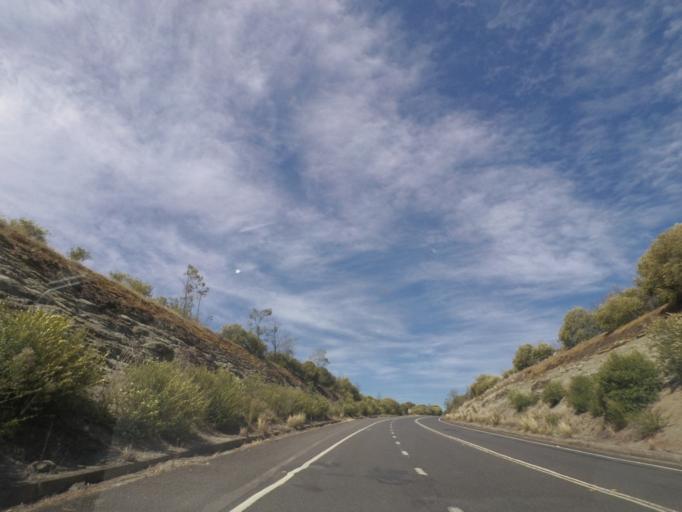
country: AU
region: New South Wales
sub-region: Wollondilly
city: Douglas Park
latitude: -34.1501
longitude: 150.6710
